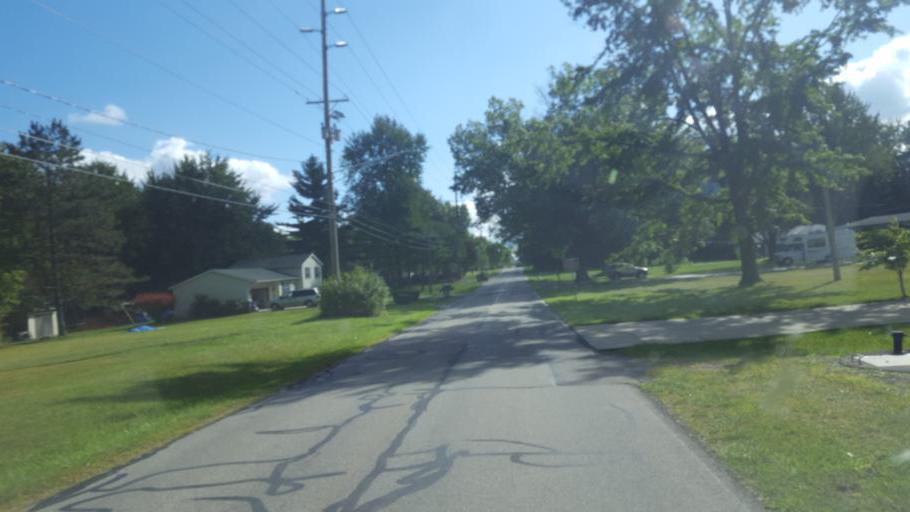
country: US
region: Ohio
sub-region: Lorain County
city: Oberlin
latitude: 41.2795
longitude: -82.2138
